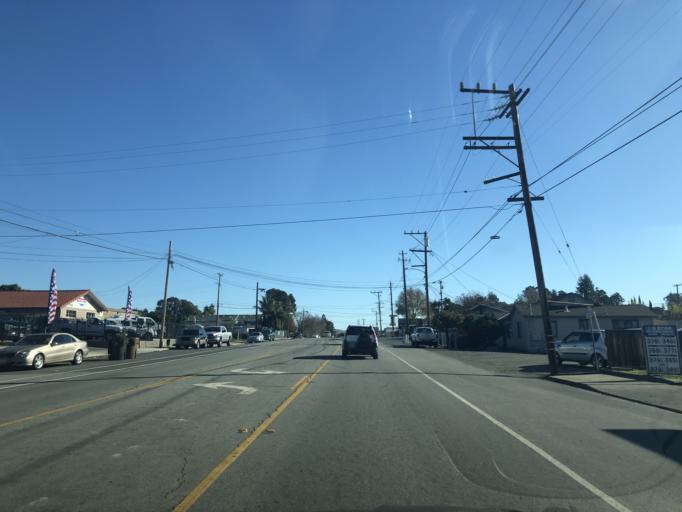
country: US
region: California
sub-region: Contra Costa County
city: Vine Hill
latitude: 38.0100
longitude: -122.0999
